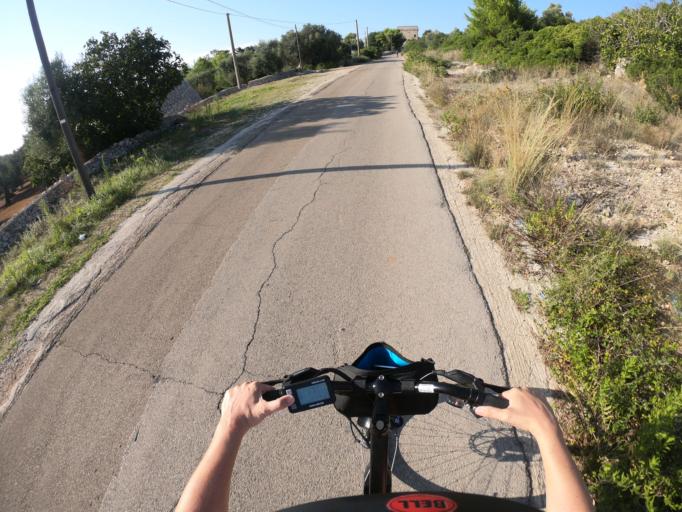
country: IT
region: Apulia
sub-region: Provincia di Lecce
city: Leuca
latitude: 39.8062
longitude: 18.3657
